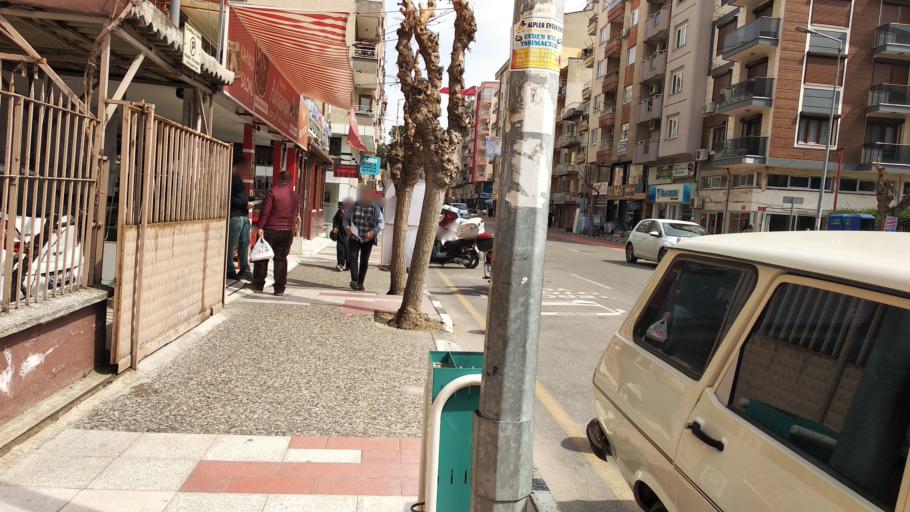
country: TR
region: Manisa
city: Manisa
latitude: 38.6131
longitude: 27.4151
